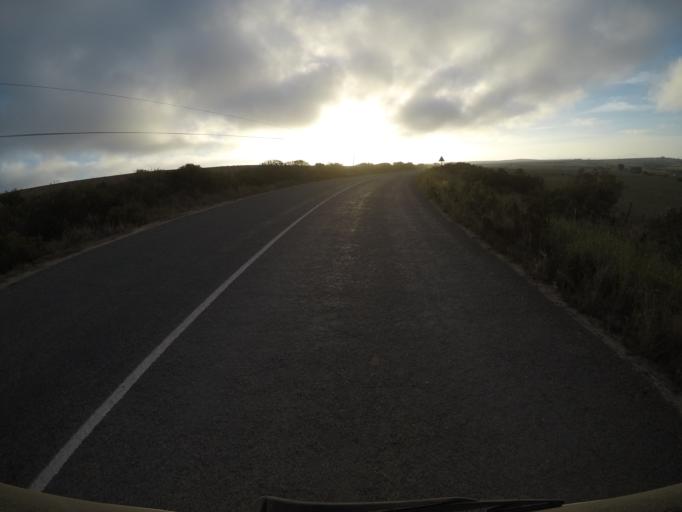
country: ZA
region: Western Cape
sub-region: Eden District Municipality
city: Mossel Bay
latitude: -34.1098
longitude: 22.0723
